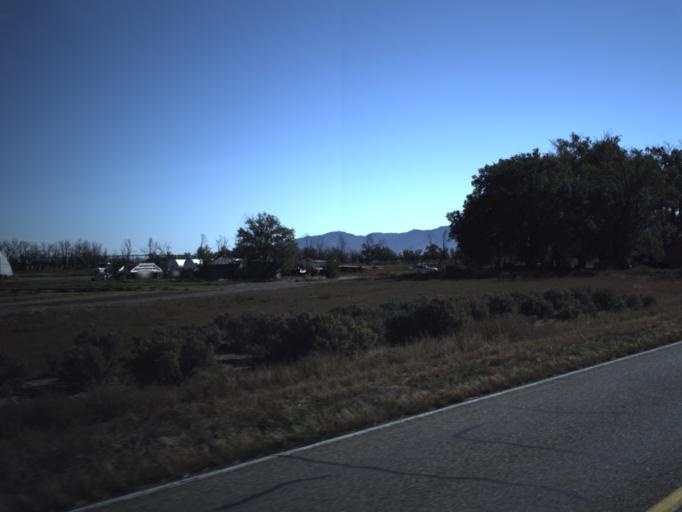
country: US
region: Utah
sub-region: Washington County
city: Enterprise
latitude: 37.7146
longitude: -113.6705
